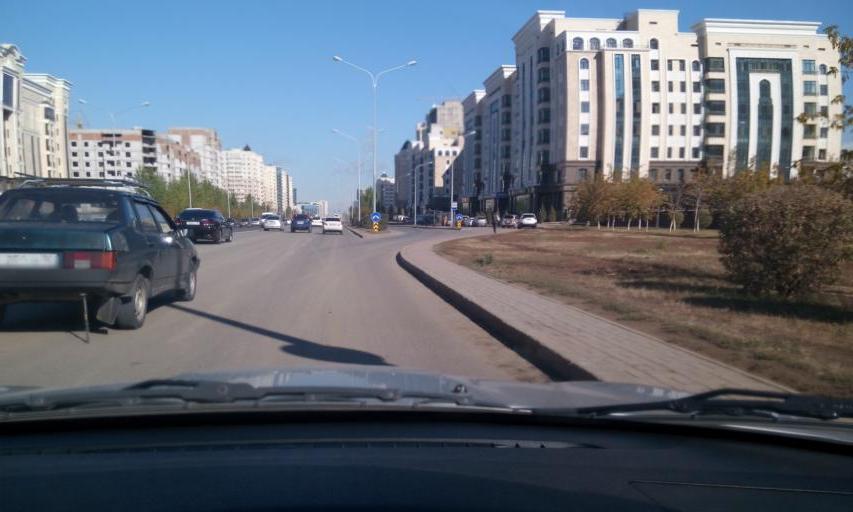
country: KZ
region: Astana Qalasy
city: Astana
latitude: 51.1088
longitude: 71.4318
